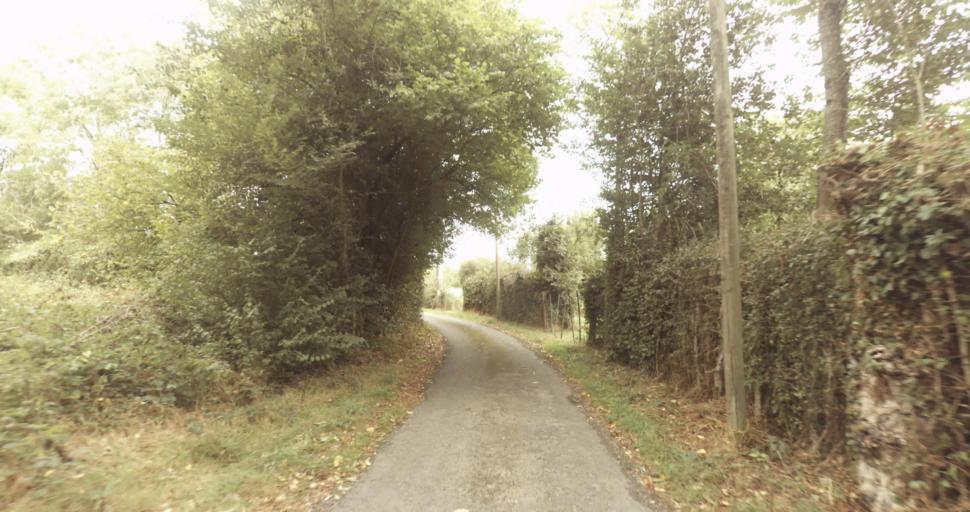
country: FR
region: Lower Normandy
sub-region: Departement de l'Orne
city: Gace
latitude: 48.8583
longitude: 0.3205
